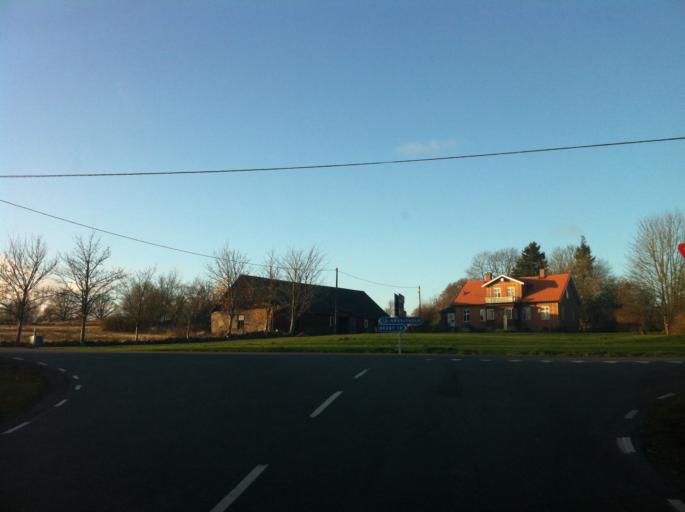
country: SE
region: Skane
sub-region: Ostra Goinge Kommun
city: Knislinge
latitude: 56.1824
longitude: 13.9870
